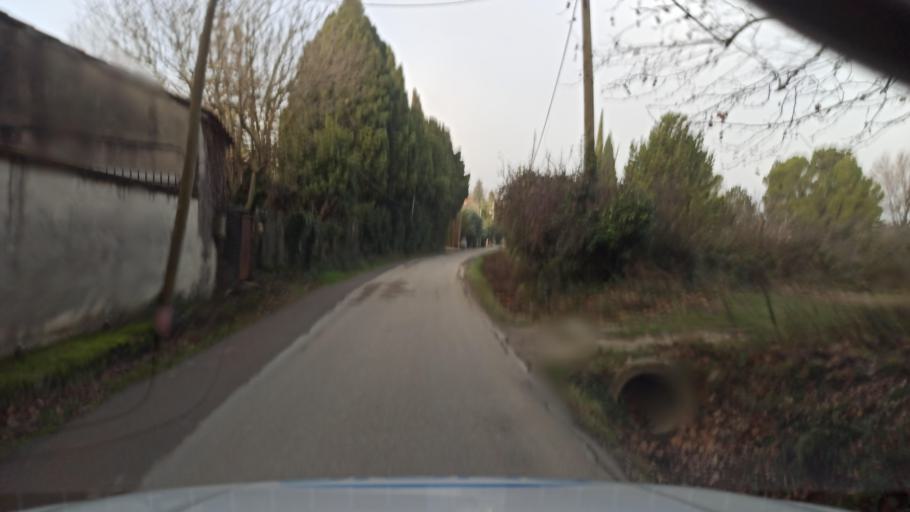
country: FR
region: Provence-Alpes-Cote d'Azur
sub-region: Departement des Bouches-du-Rhone
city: Rognonas
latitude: 43.8945
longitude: 4.7911
